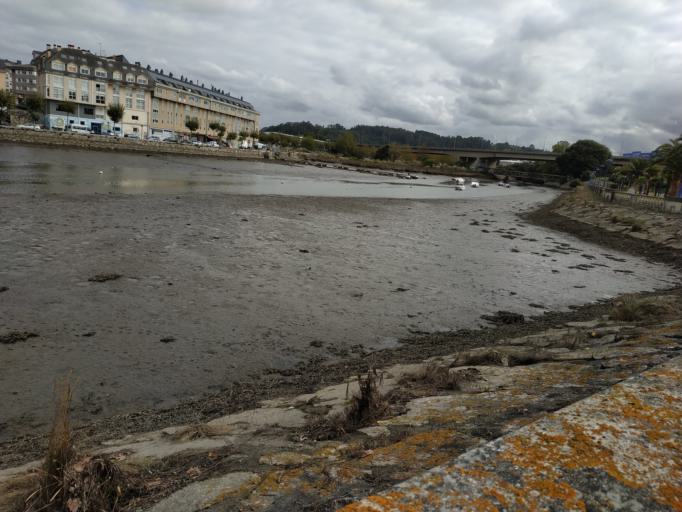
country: ES
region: Galicia
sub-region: Provincia da Coruna
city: Cambre
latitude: 43.3144
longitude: -8.3605
